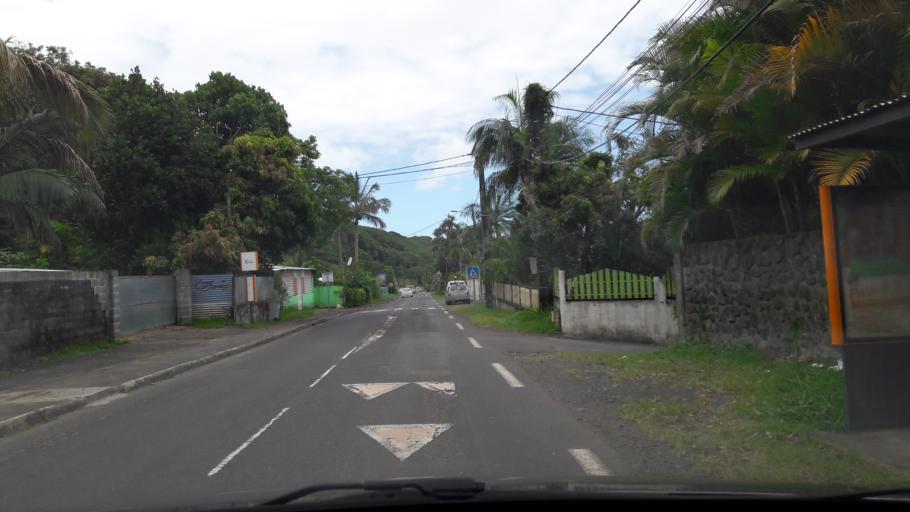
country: RE
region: Reunion
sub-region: Reunion
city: Saint-Andre
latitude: -20.9825
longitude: 55.6293
